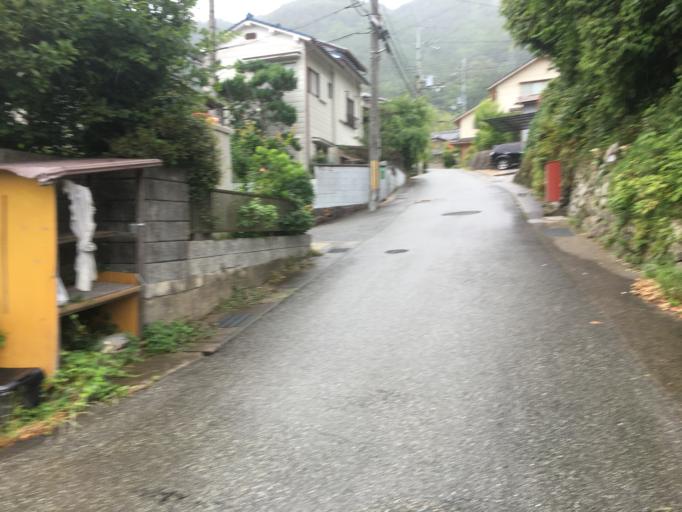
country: JP
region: Kyoto
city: Kameoka
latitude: 35.0100
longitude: 135.6110
